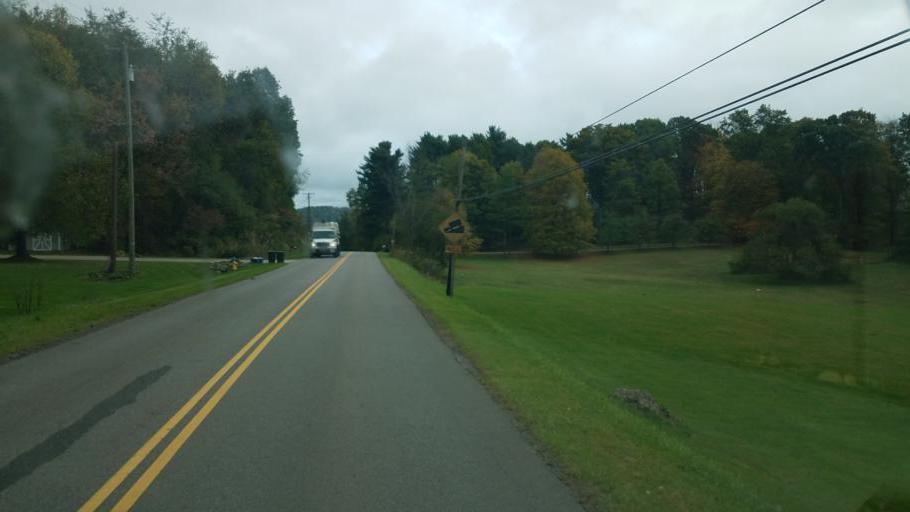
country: US
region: Ohio
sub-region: Ashland County
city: Loudonville
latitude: 40.6296
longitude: -82.2417
